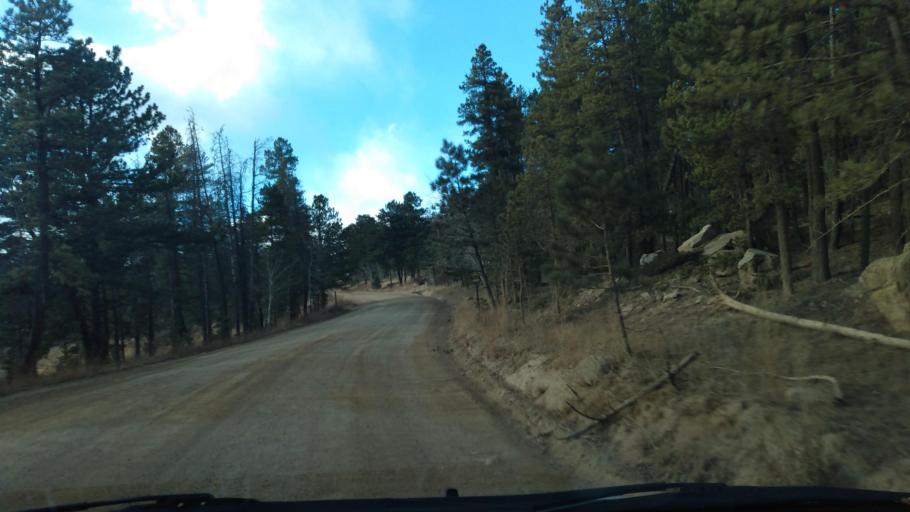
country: US
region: Colorado
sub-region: Boulder County
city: Nederland
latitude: 39.9510
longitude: -105.4521
